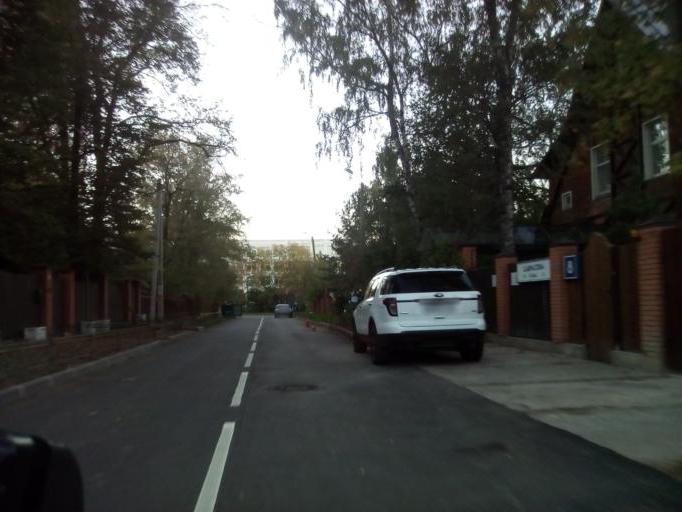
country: RU
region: Moscow
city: Sokol
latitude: 55.8046
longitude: 37.5020
